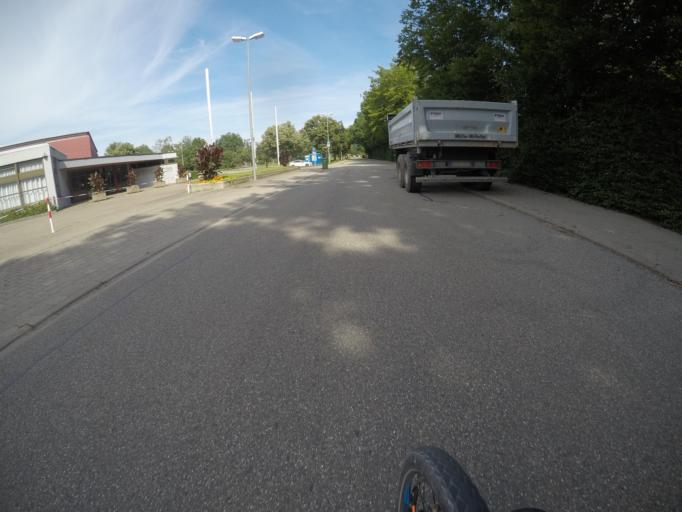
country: DE
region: Baden-Wuerttemberg
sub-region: Karlsruhe Region
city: Otisheim
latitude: 48.9653
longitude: 8.8034
